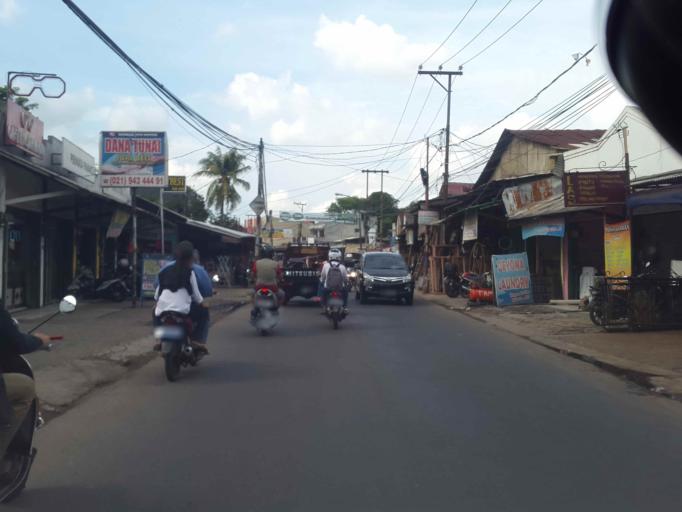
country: ID
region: West Java
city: Bekasi
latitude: -6.2955
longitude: 106.9205
